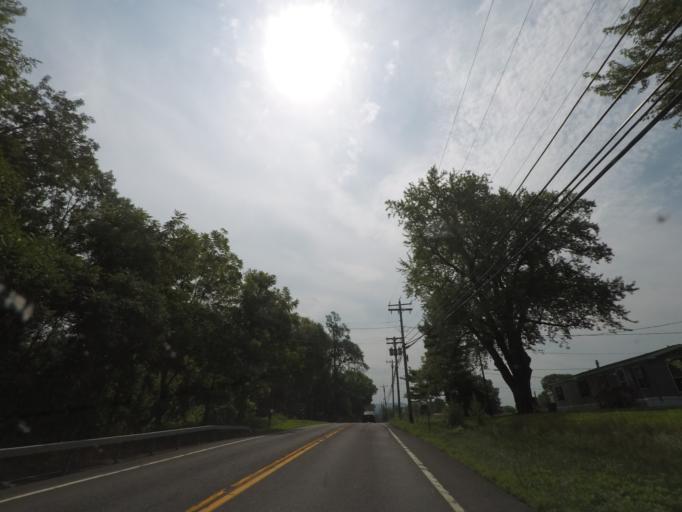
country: US
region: New York
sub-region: Saratoga County
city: Waterford
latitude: 42.8391
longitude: -73.6742
